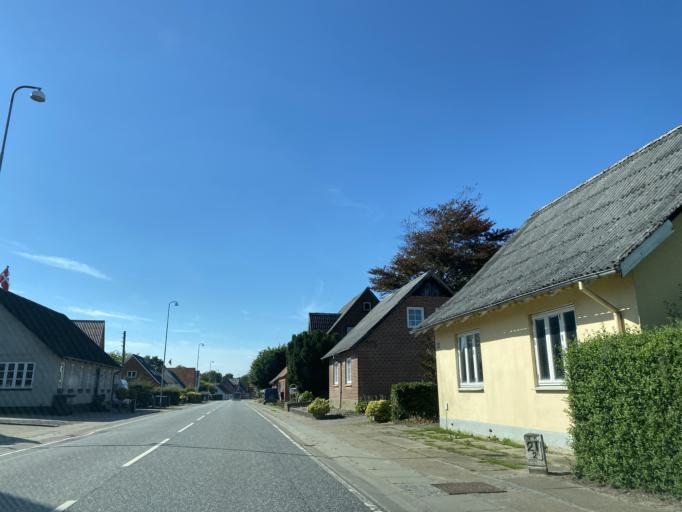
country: DK
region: Central Jutland
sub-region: Hedensted Kommune
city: Torring
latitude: 55.8591
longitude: 9.4210
